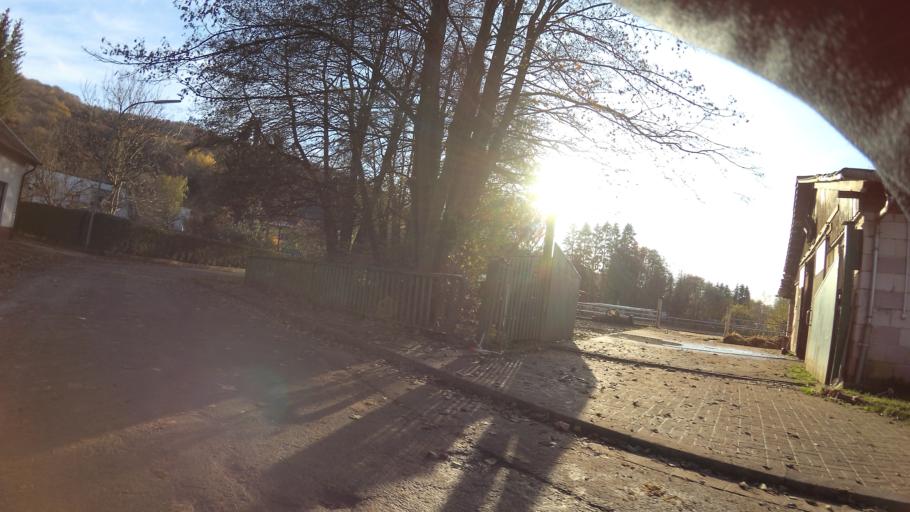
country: DE
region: Saarland
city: Namborn
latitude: 49.5277
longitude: 7.1752
